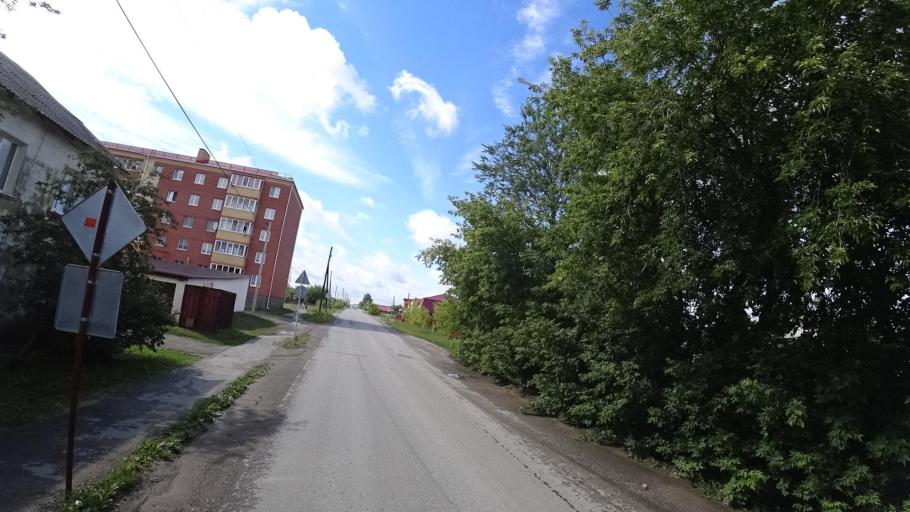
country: RU
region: Sverdlovsk
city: Kamyshlov
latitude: 56.8374
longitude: 62.7345
